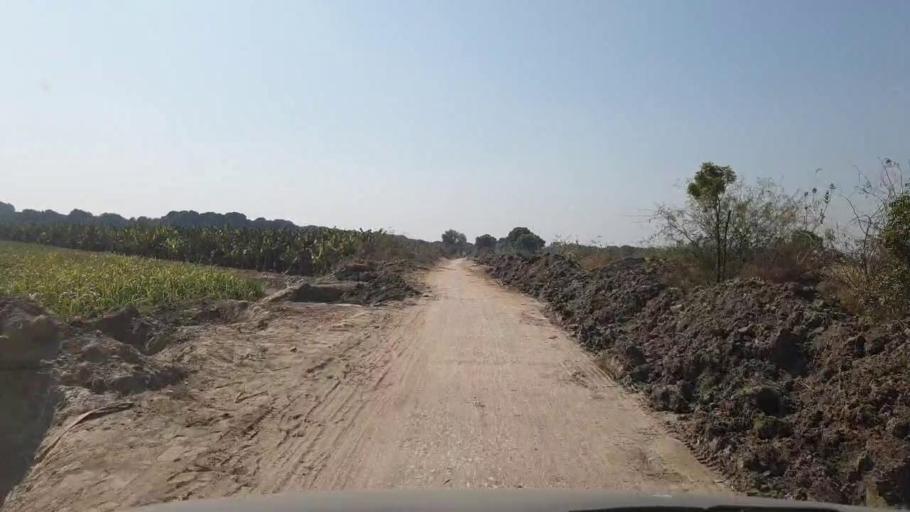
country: PK
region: Sindh
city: Tando Jam
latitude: 25.4232
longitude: 68.6290
